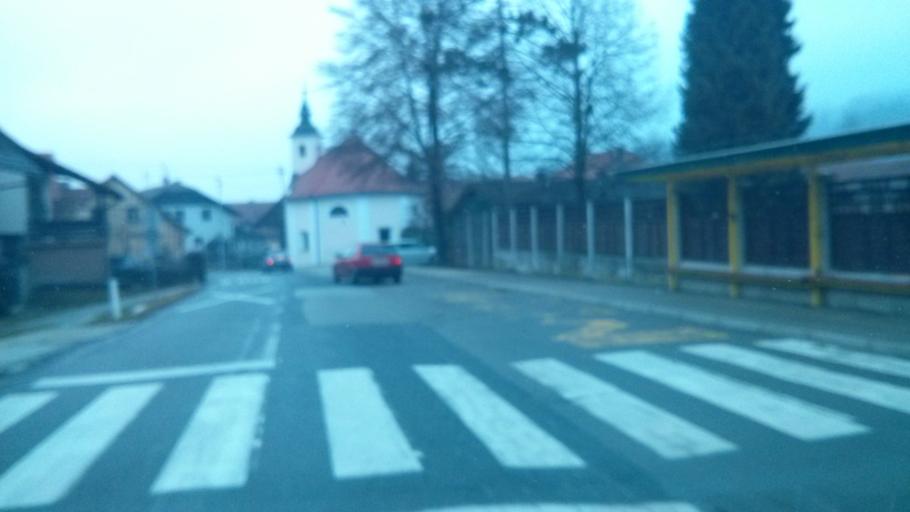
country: SI
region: Smartno pri Litiji
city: Smartno pri Litiji
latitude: 46.0426
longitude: 14.8434
